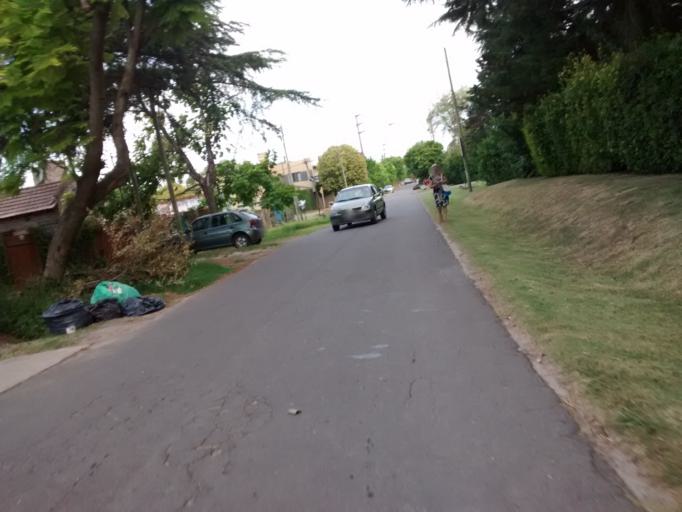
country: AR
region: Buenos Aires
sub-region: Partido de La Plata
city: La Plata
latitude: -34.8630
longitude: -58.0570
